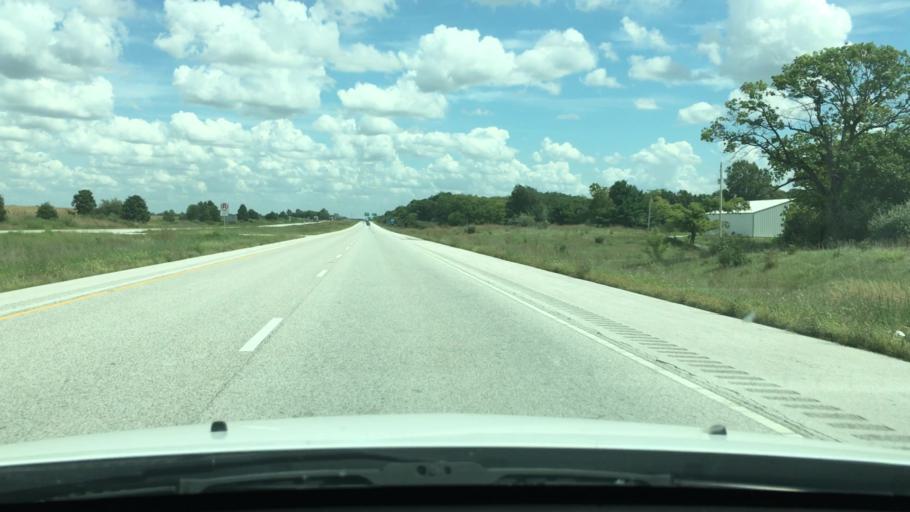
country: US
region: Illinois
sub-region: Morgan County
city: South Jacksonville
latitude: 39.6802
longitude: -90.3126
